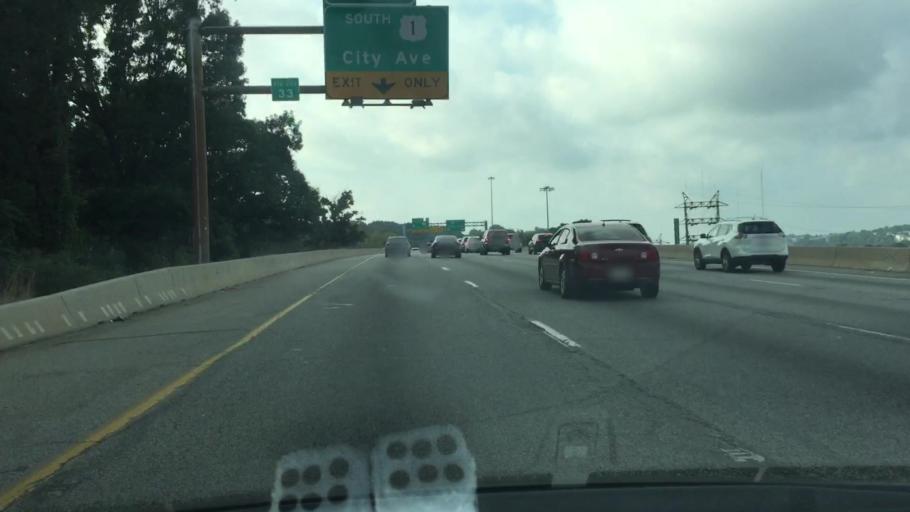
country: US
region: Pennsylvania
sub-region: Montgomery County
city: Bala-Cynwyd
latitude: 40.0095
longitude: -75.2055
